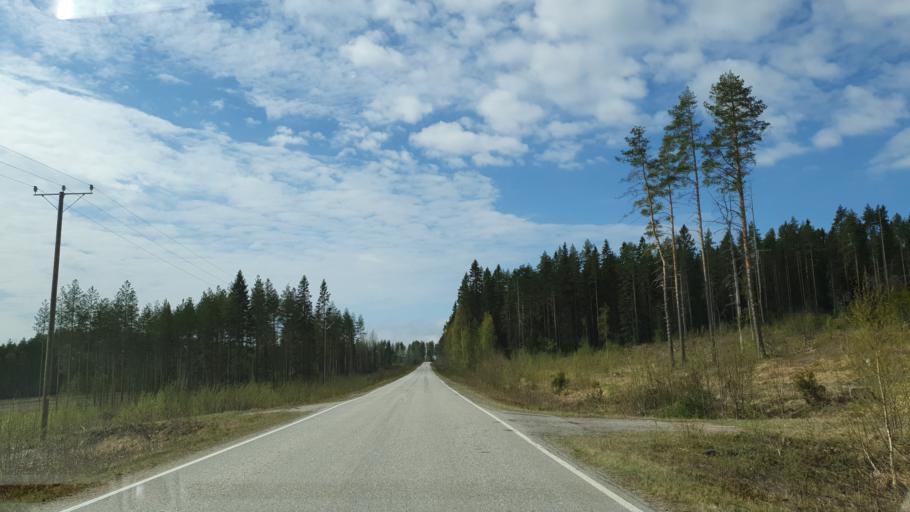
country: FI
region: Kainuu
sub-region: Kehys-Kainuu
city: Kuhmo
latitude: 64.1213
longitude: 29.6809
